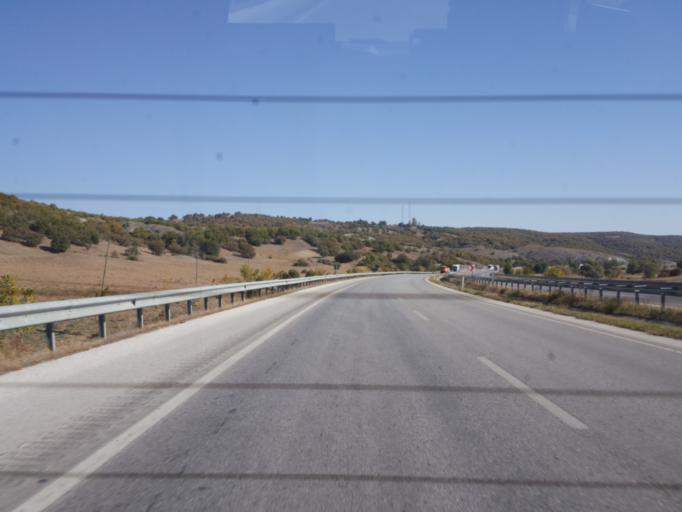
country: TR
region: Corum
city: Alaca
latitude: 40.3076
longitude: 34.6559
